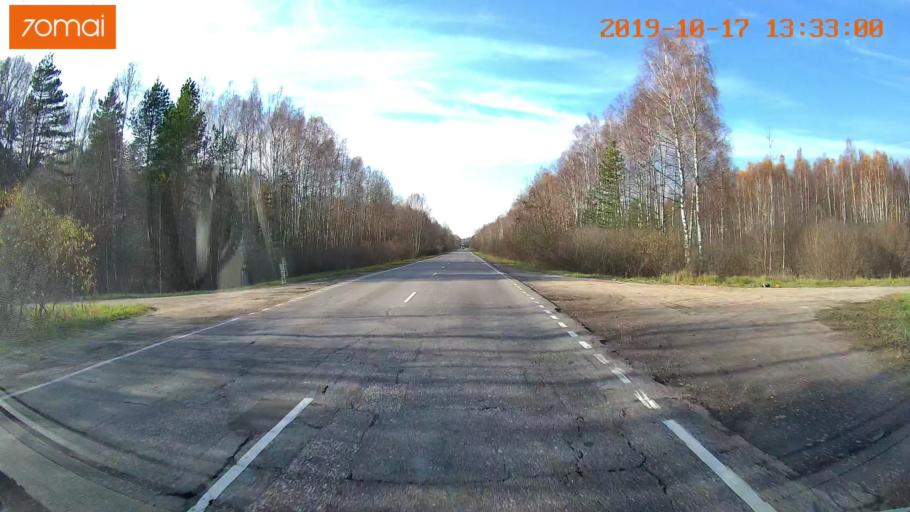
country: RU
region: Vladimir
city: Velikodvorskiy
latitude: 55.1402
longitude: 40.7515
